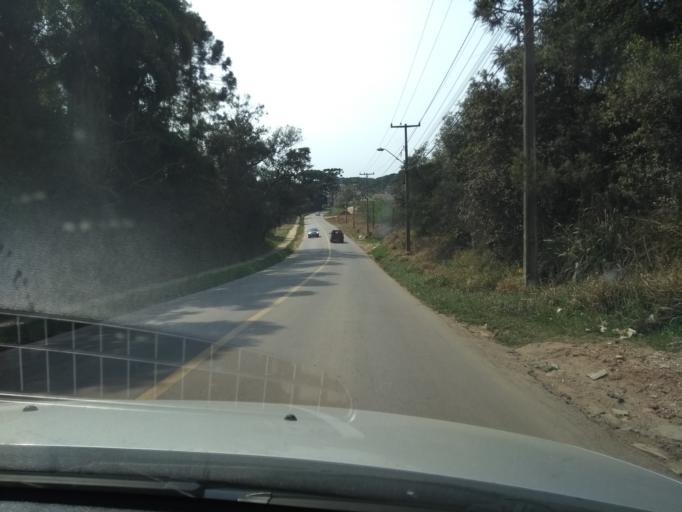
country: BR
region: Parana
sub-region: Araucaria
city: Araucaria
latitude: -25.6131
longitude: -49.3405
